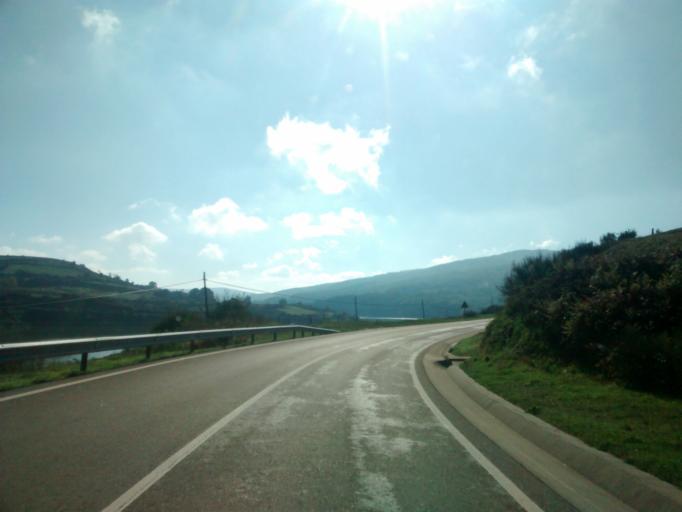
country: ES
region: Cantabria
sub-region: Provincia de Cantabria
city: Reinosa
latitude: 42.9841
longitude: -4.1058
